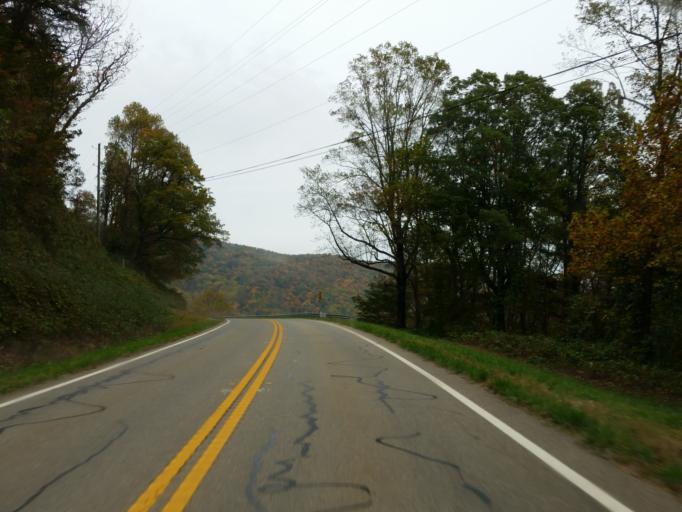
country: US
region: Georgia
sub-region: Pickens County
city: Jasper
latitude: 34.5285
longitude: -84.3982
